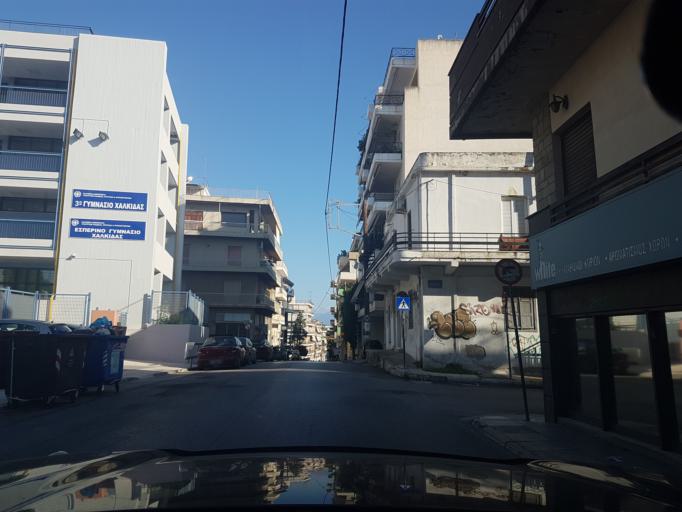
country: GR
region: Central Greece
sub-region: Nomos Evvoias
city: Chalkida
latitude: 38.4661
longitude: 23.6023
